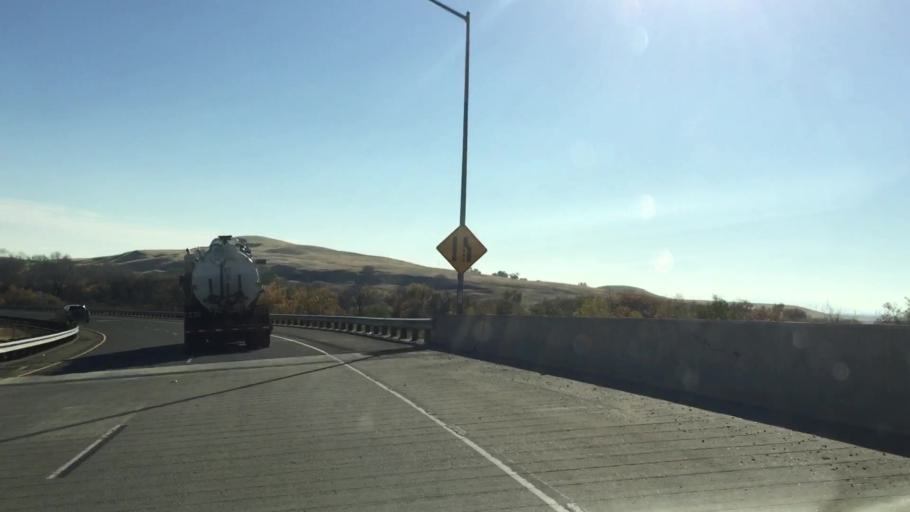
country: US
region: California
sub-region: Butte County
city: Thermalito
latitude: 39.5816
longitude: -121.6226
